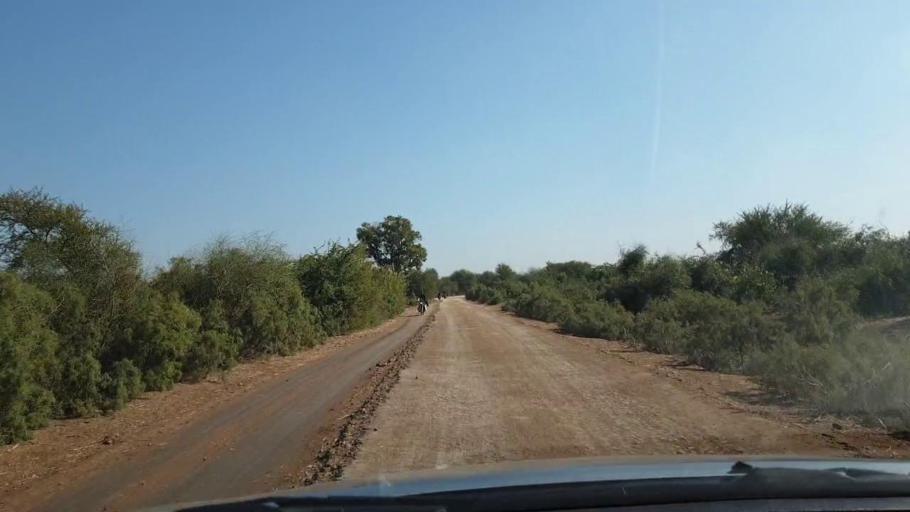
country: PK
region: Sindh
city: Jhol
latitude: 25.9262
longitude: 68.9303
